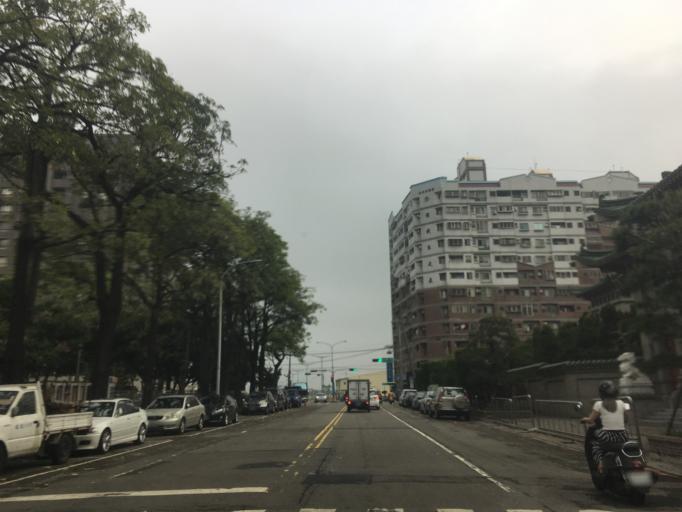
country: TW
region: Taiwan
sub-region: Taichung City
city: Taichung
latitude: 24.1761
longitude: 120.6767
